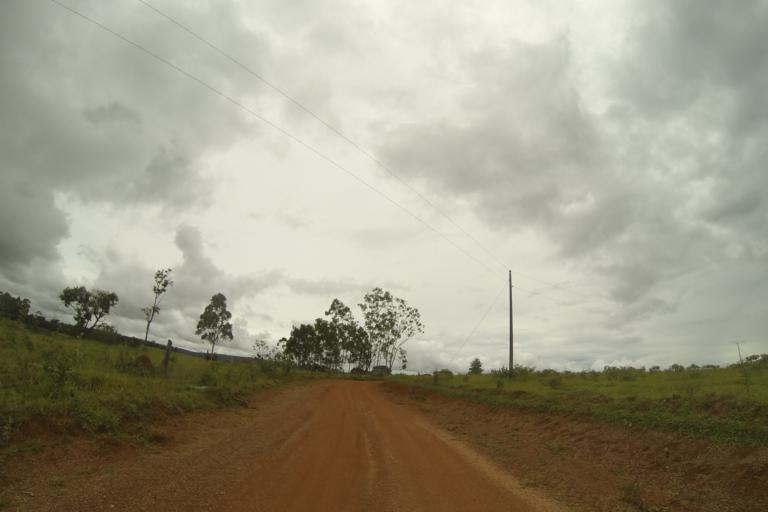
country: BR
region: Minas Gerais
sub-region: Ibia
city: Ibia
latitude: -19.7294
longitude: -46.5993
